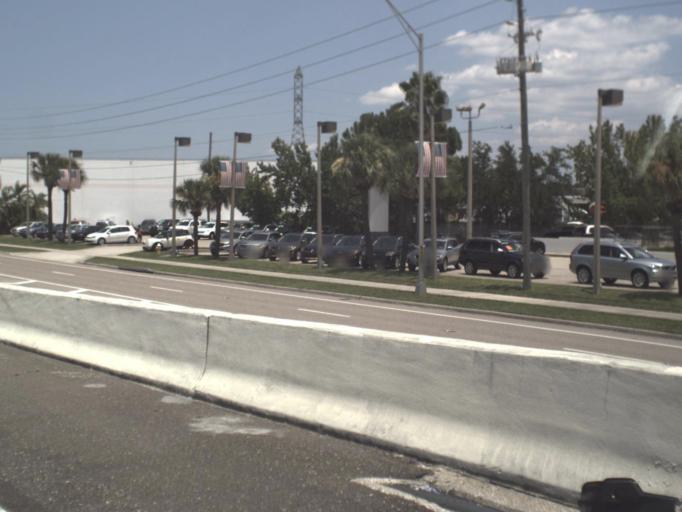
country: US
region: Florida
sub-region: Pinellas County
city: South Highpoint
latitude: 27.8958
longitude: -82.7238
